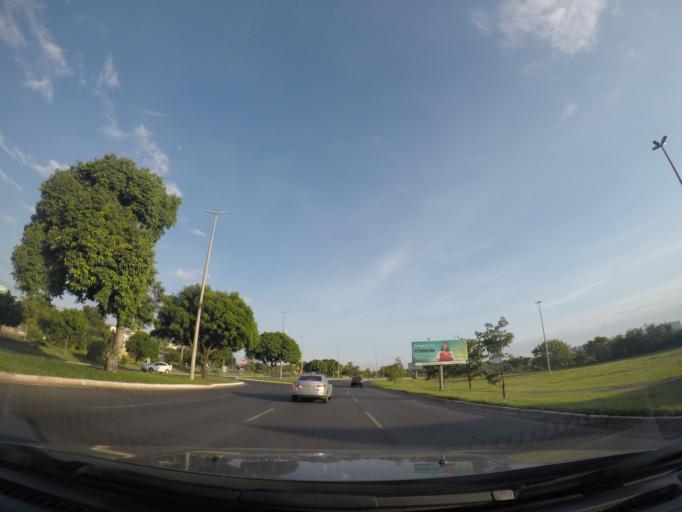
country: BR
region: Federal District
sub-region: Brasilia
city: Brasilia
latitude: -15.8389
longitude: -47.9664
